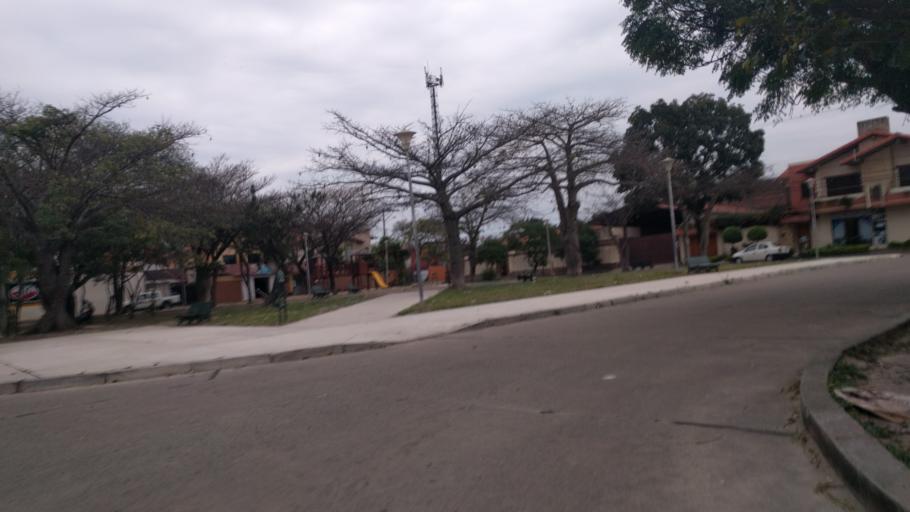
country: BO
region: Santa Cruz
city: Santa Cruz de la Sierra
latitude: -17.8111
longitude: -63.2042
